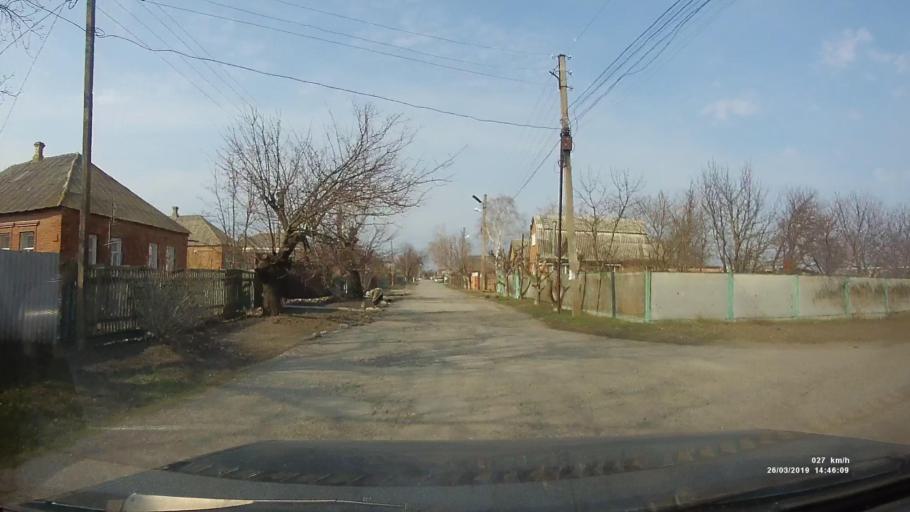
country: RU
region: Rostov
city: Novobessergenovka
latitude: 47.1852
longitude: 38.8608
